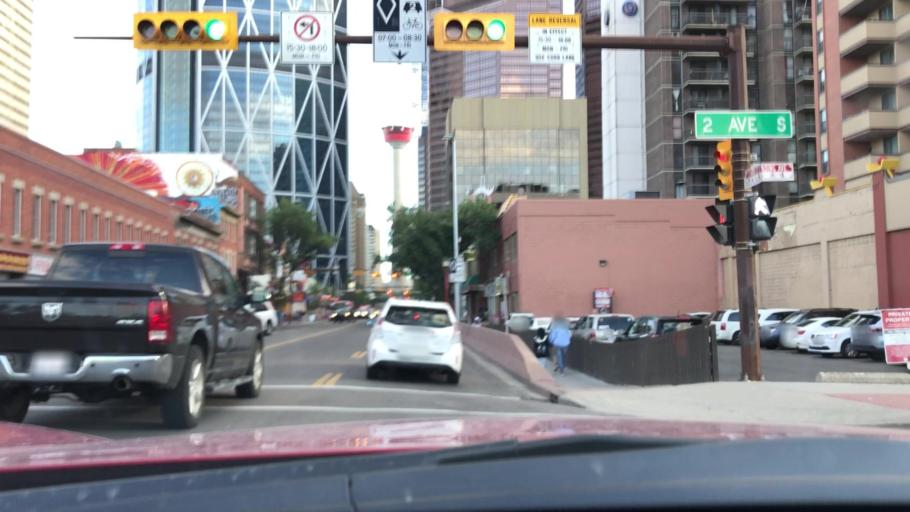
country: CA
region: Alberta
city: Calgary
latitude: 51.0513
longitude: -114.0627
